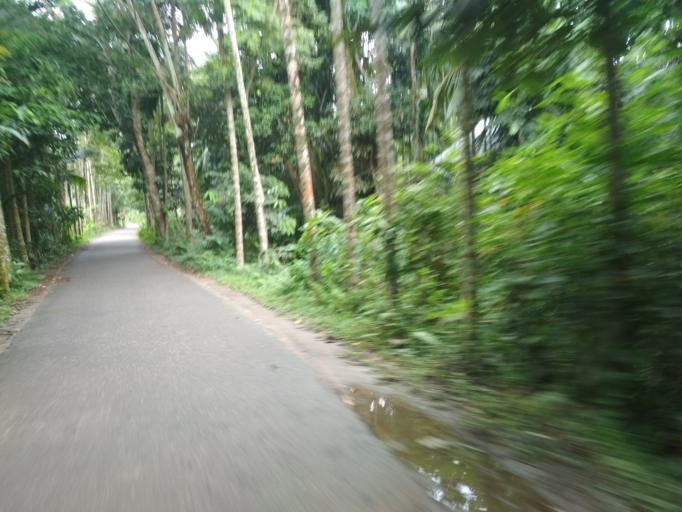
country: BD
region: Chittagong
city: Lakshmipur
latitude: 22.9674
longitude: 90.7970
